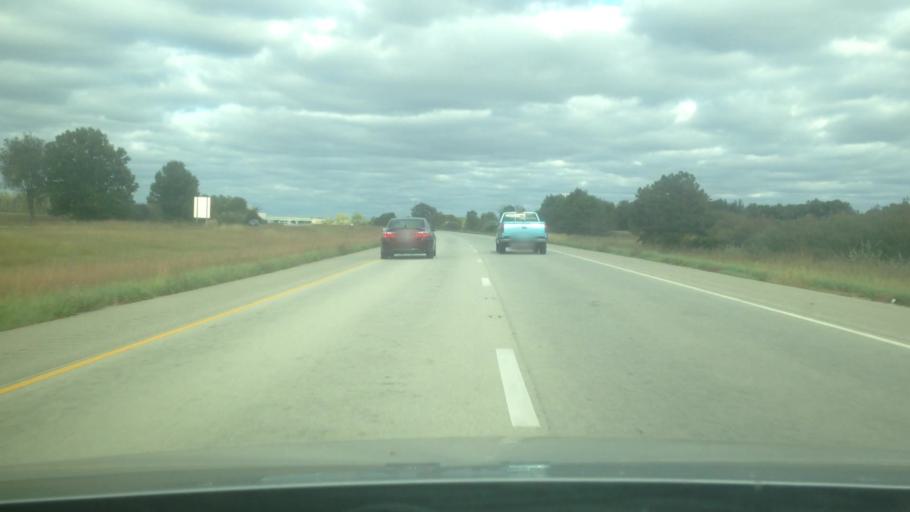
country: US
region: Illinois
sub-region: Macon County
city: Forsyth
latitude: 39.9128
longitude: -88.8702
